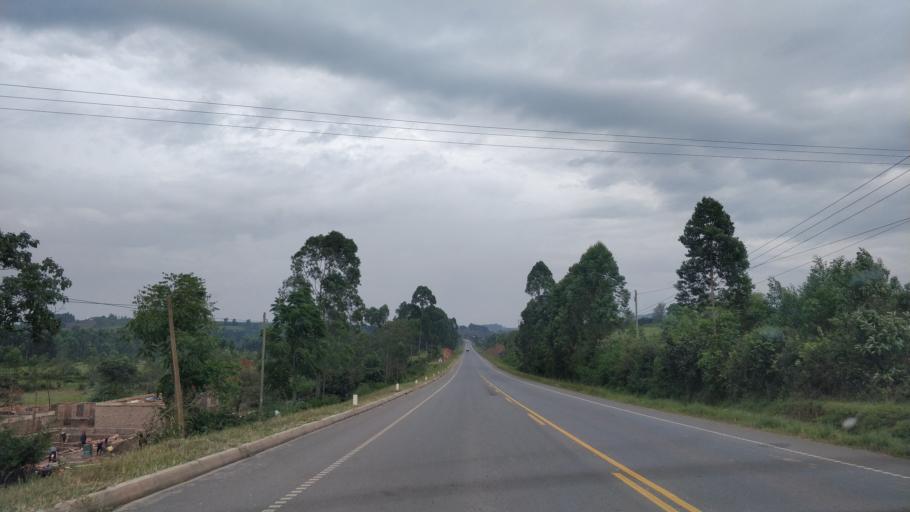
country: UG
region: Western Region
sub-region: Sheema District
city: Kibingo
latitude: -0.6583
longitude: 30.4680
